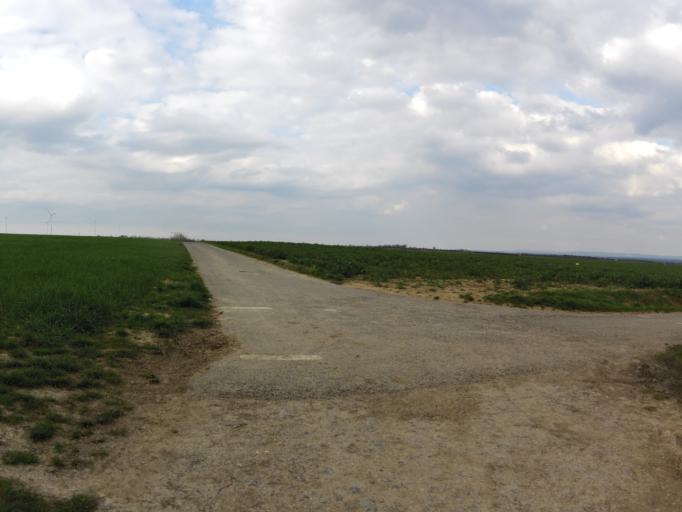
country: DE
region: Bavaria
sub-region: Regierungsbezirk Unterfranken
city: Buchbrunn
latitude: 49.7392
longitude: 10.1211
